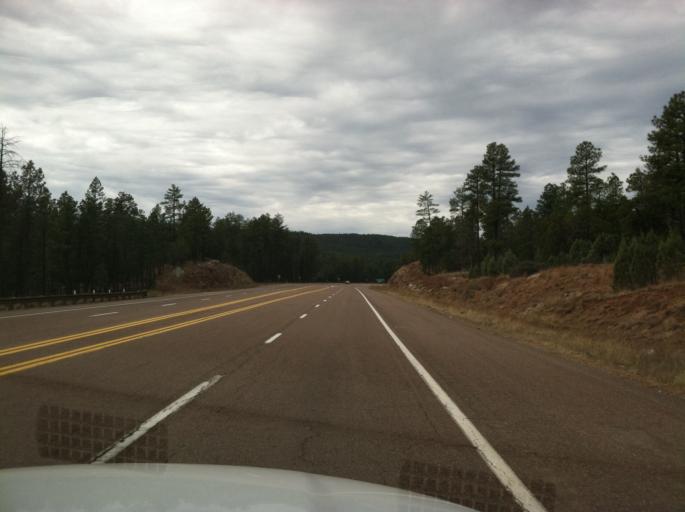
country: US
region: Arizona
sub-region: Gila County
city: Star Valley
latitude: 34.2957
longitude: -110.9681
